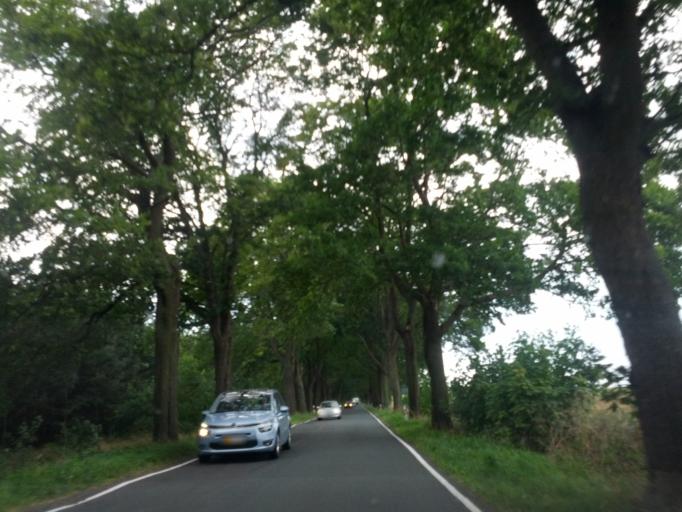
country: DE
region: Brandenburg
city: Kremmen
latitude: 52.7456
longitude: 12.9314
